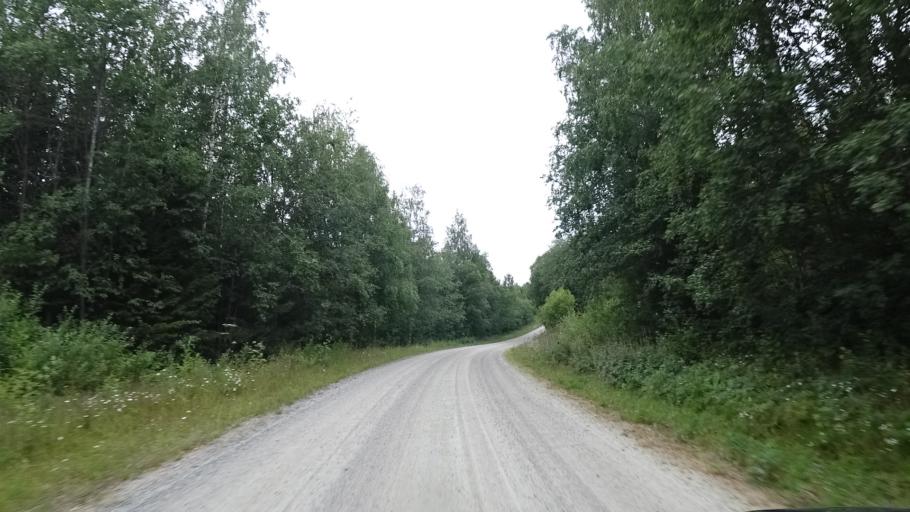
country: FI
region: North Karelia
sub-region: Joensuu
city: Eno
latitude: 63.1767
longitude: 30.5487
